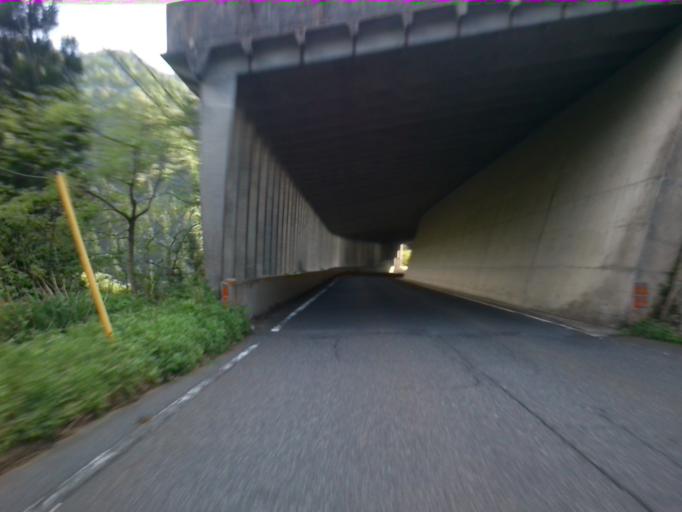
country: JP
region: Kyoto
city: Miyazu
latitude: 35.7026
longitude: 135.1870
